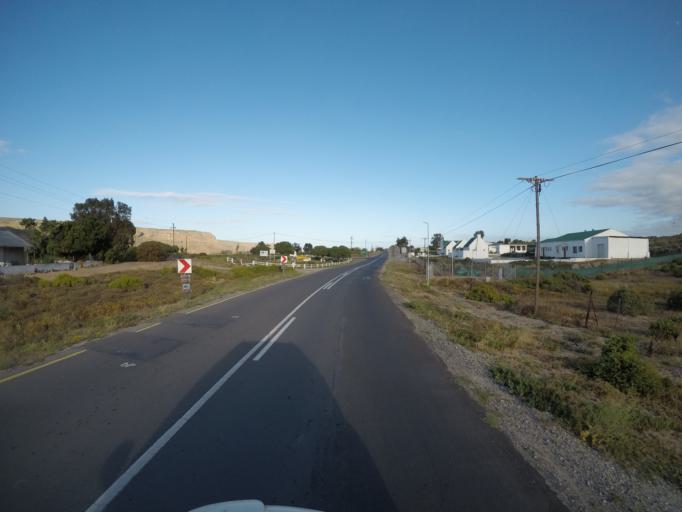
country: ZA
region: Western Cape
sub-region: West Coast District Municipality
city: Clanwilliam
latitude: -32.3132
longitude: 18.3568
